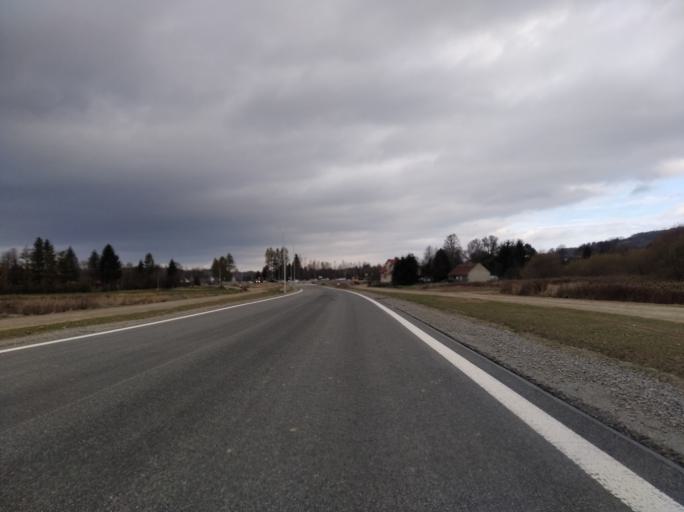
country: PL
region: Subcarpathian Voivodeship
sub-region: Powiat strzyzowski
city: Strzyzow
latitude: 49.8726
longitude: 21.7653
